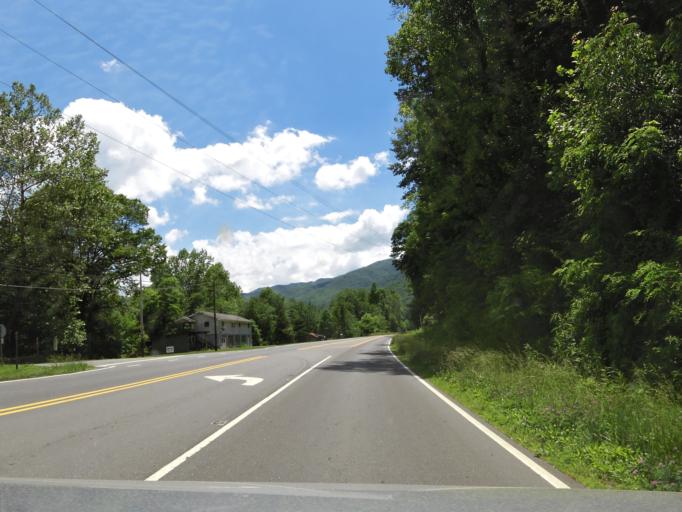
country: US
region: North Carolina
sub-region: Graham County
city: Robbinsville
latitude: 35.3077
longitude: -83.7947
